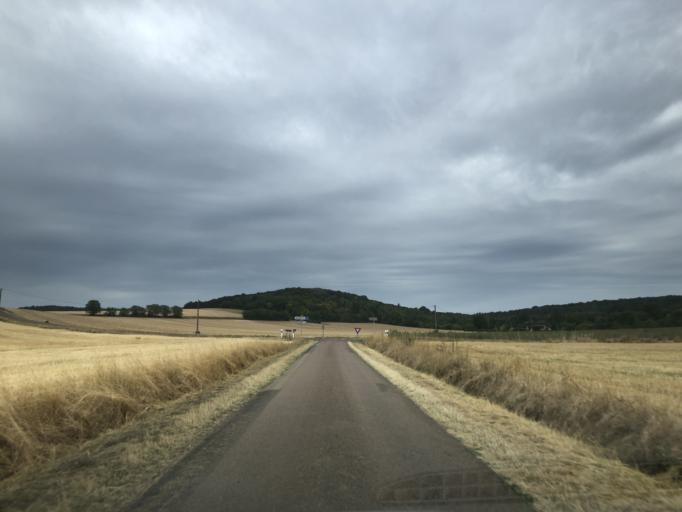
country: FR
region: Bourgogne
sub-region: Departement de l'Yonne
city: Aillant-sur-Tholon
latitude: 47.9052
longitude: 3.3348
